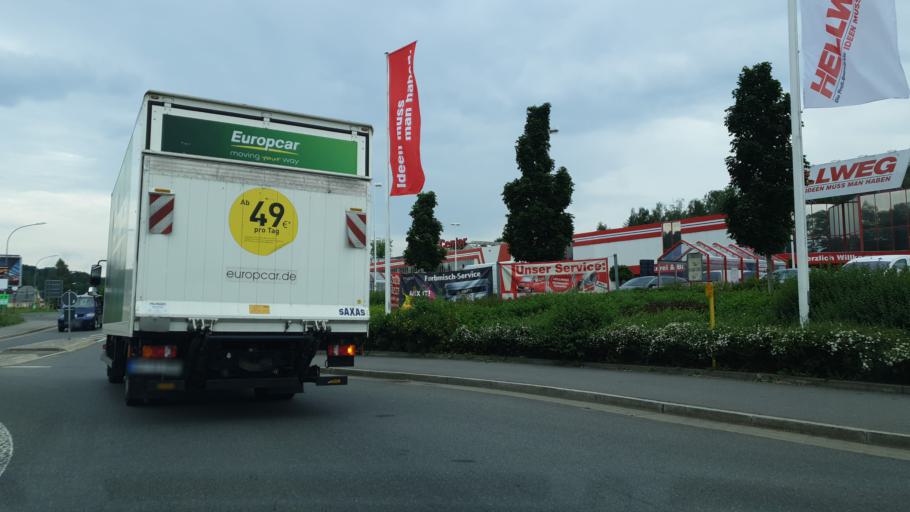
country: DE
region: Saxony
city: Rodewisch
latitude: 50.5413
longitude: 12.3952
